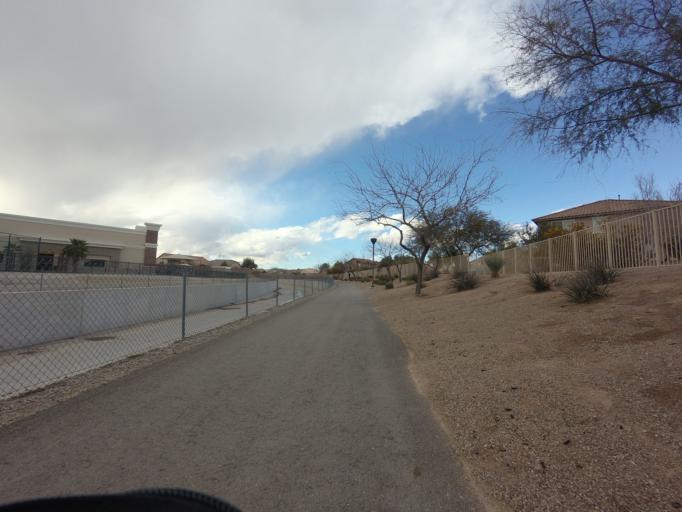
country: US
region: Nevada
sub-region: Clark County
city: North Las Vegas
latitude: 36.2625
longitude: -115.1857
